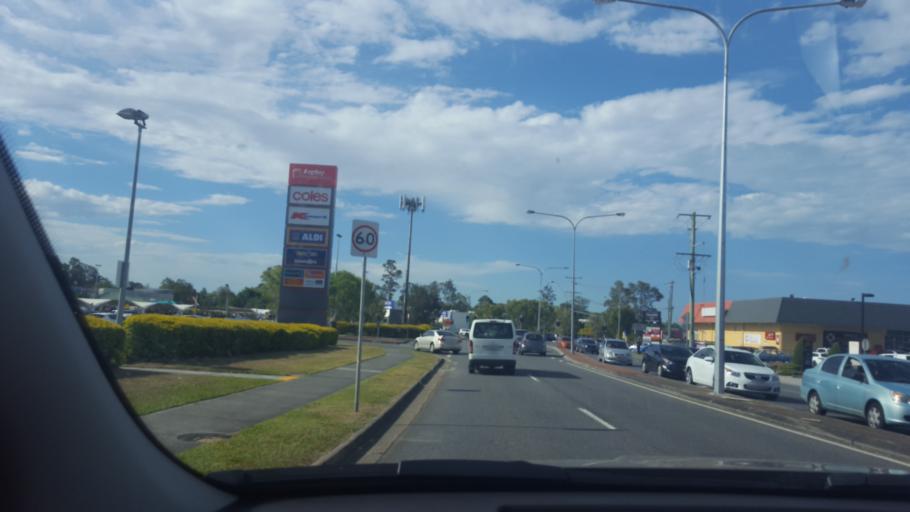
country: AU
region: Queensland
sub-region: Brisbane
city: Chermside West
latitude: -27.3635
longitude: 153.0156
